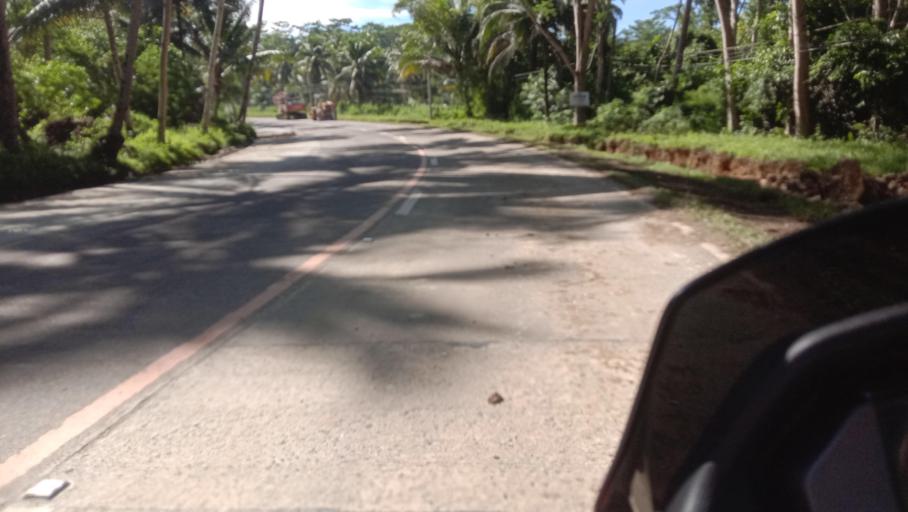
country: PH
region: Caraga
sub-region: Province of Surigao del Sur
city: Barobo
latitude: 8.5373
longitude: 126.0983
